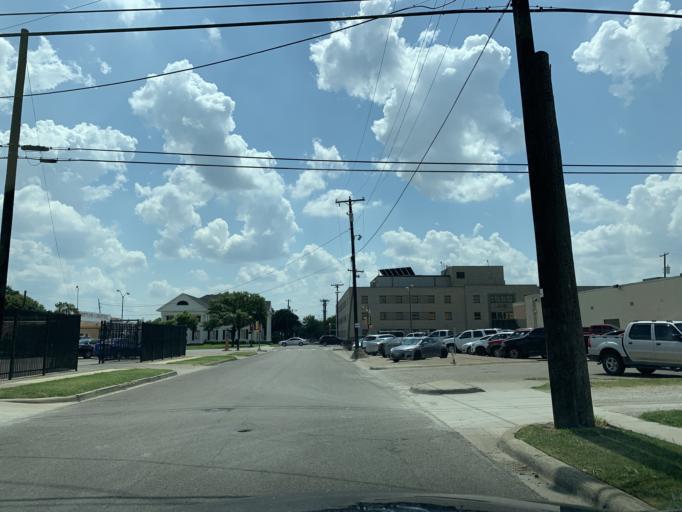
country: US
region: Texas
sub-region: Dallas County
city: Dallas
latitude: 32.7461
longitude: -96.8197
